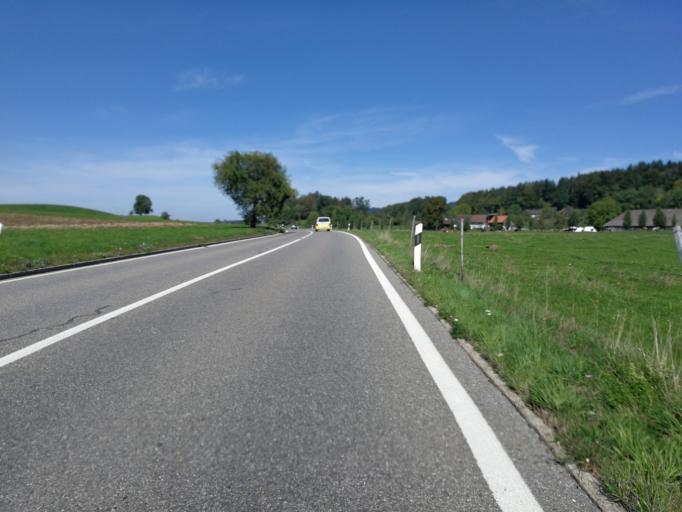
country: CH
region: Zurich
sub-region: Bezirk Hinwil
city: Hinwil
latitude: 47.3105
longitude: 8.8292
